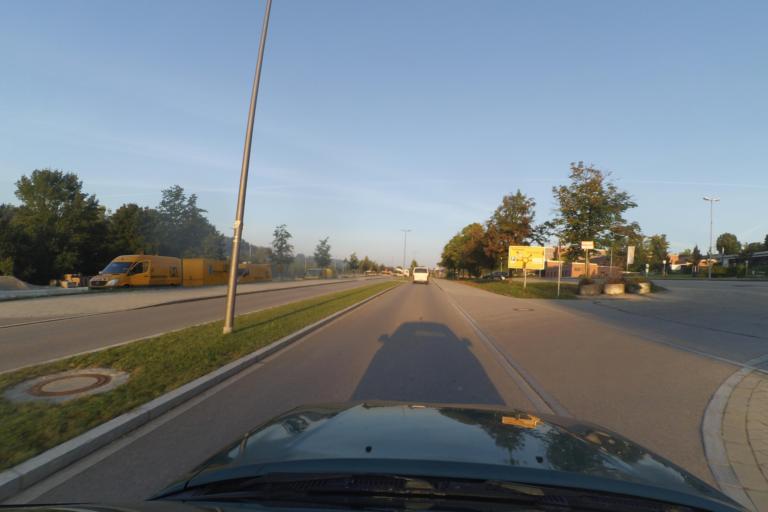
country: DE
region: Bavaria
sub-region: Lower Bavaria
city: Mainburg
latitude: 48.6490
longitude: 11.7714
